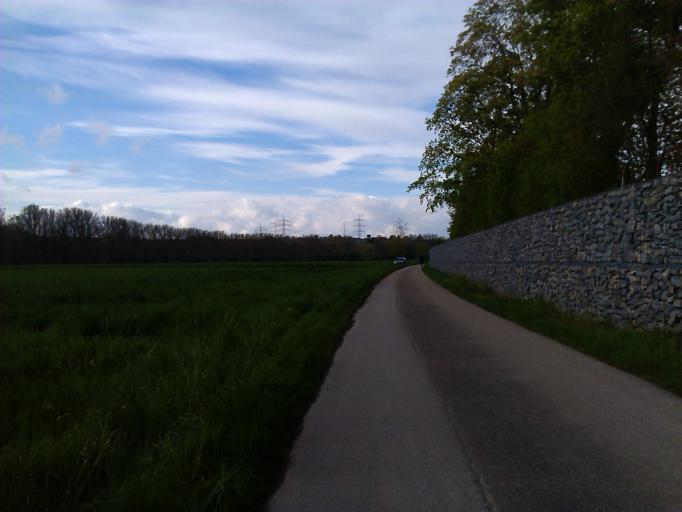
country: DE
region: Baden-Wuerttemberg
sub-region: Regierungsbezirk Stuttgart
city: Nordheim
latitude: 49.1029
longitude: 9.1522
